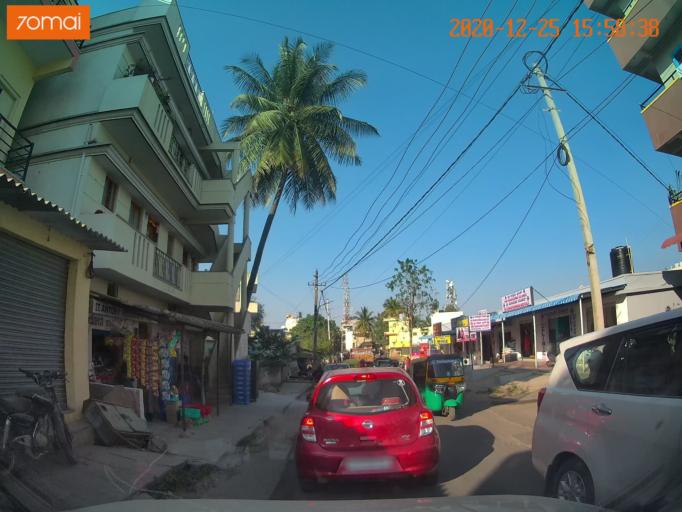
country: IN
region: Karnataka
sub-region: Bangalore Urban
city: Bangalore
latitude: 12.8722
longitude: 77.6246
